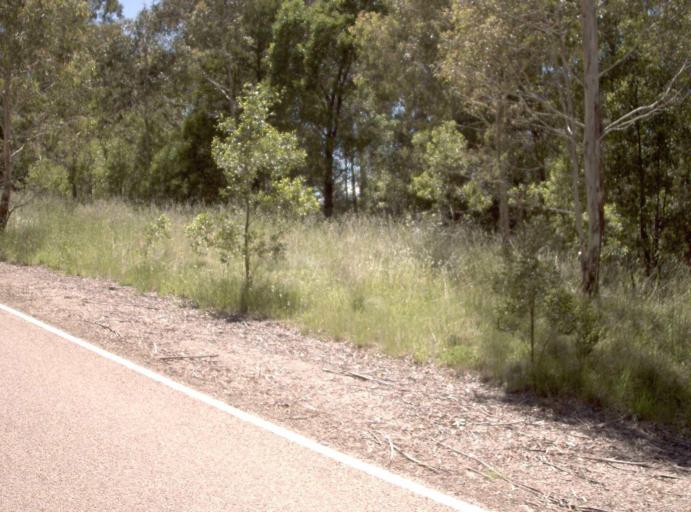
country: AU
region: Victoria
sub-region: East Gippsland
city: Lakes Entrance
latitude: -37.2155
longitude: 148.2679
